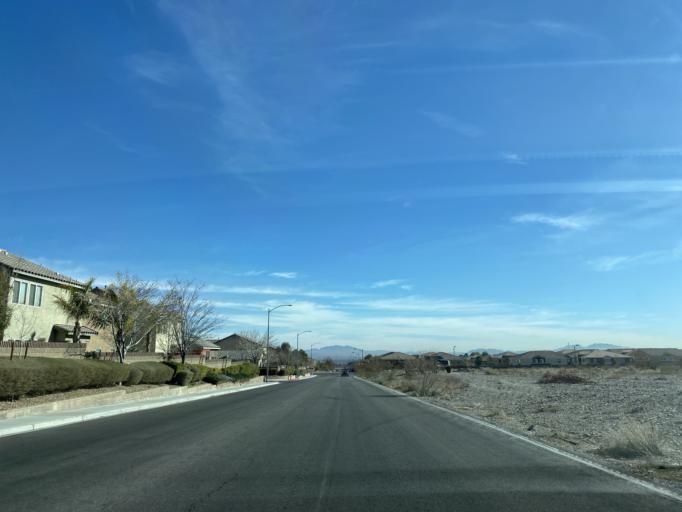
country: US
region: Nevada
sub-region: Clark County
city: Summerlin South
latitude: 36.3029
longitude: -115.3034
